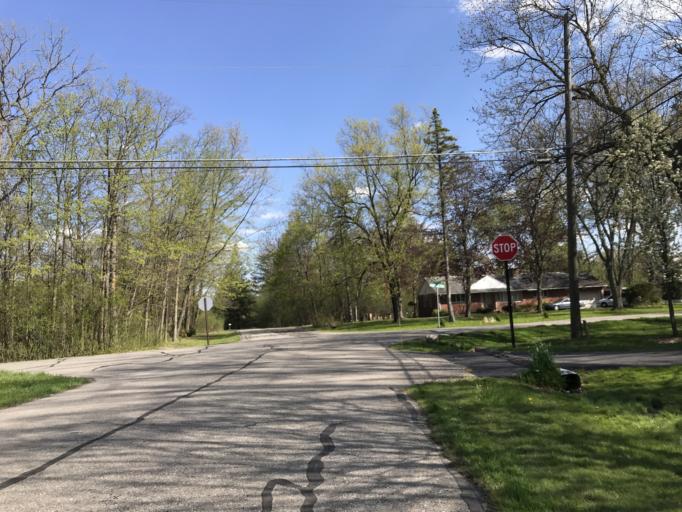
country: US
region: Michigan
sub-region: Oakland County
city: Farmington
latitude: 42.4764
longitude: -83.3317
